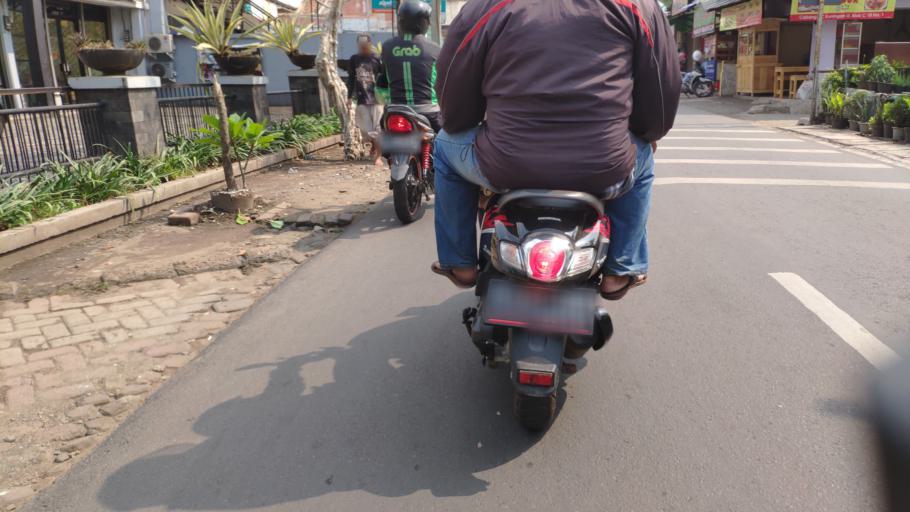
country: ID
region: West Java
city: Depok
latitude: -6.3125
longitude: 106.8257
